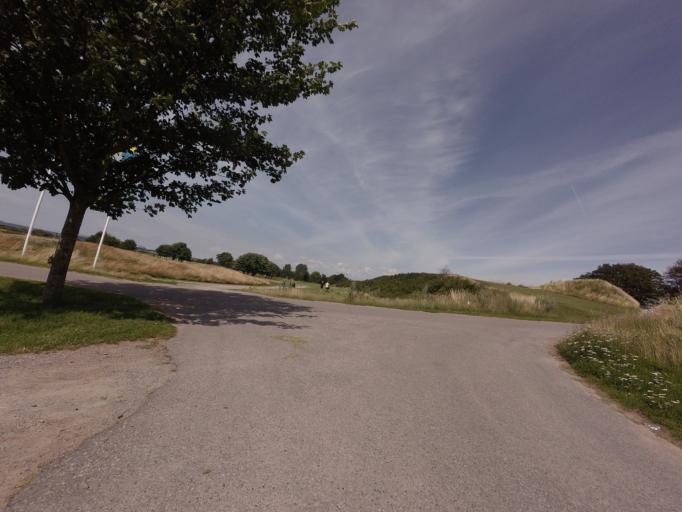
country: SE
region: Skane
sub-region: Helsingborg
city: Rydeback
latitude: 55.9755
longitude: 12.7586
